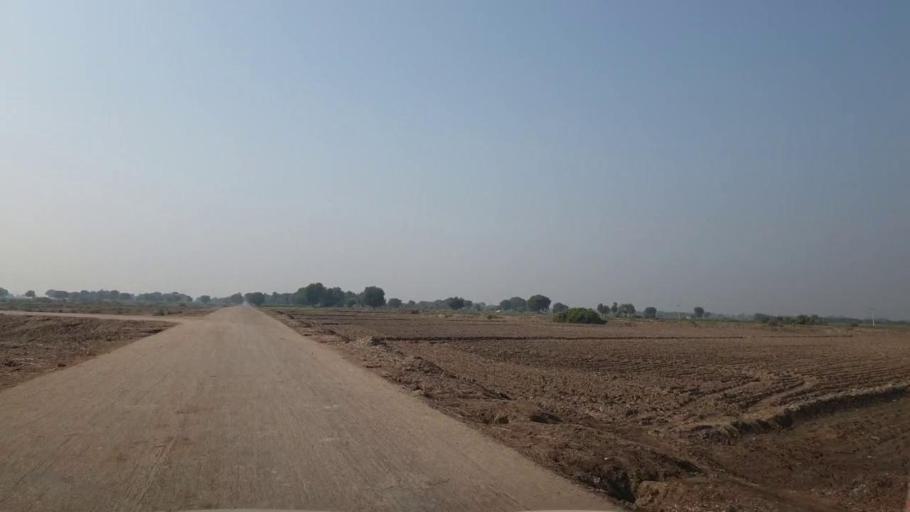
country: PK
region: Sindh
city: Bhan
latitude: 26.5239
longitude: 67.8100
